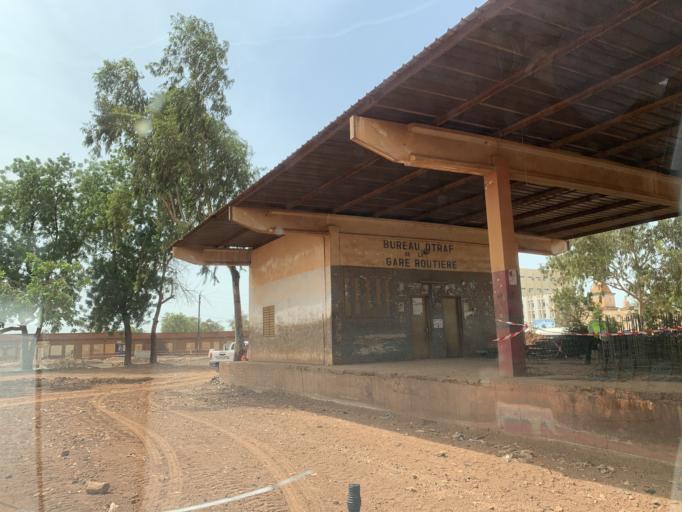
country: BF
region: Centre
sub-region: Kadiogo Province
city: Ouagadougou
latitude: 12.3338
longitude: -1.5163
